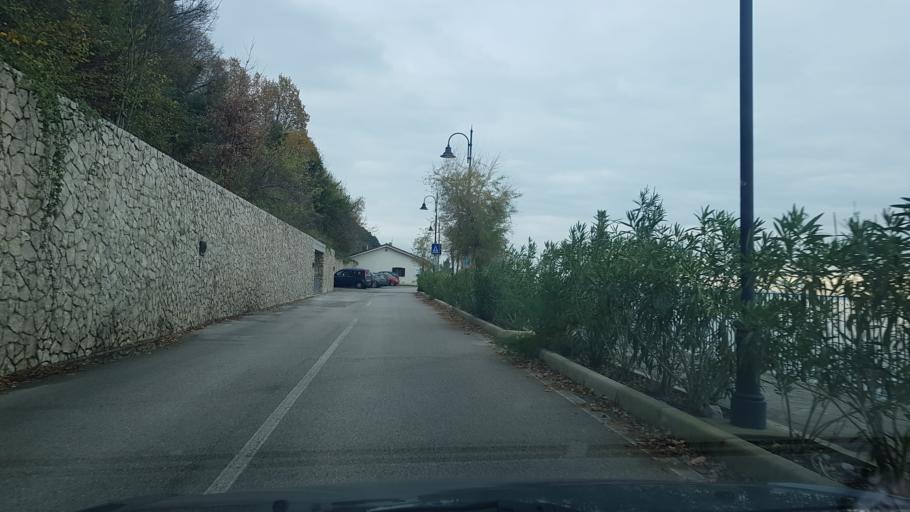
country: IT
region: Friuli Venezia Giulia
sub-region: Provincia di Trieste
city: Sistiana-Visogliano
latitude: 45.7669
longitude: 13.6335
